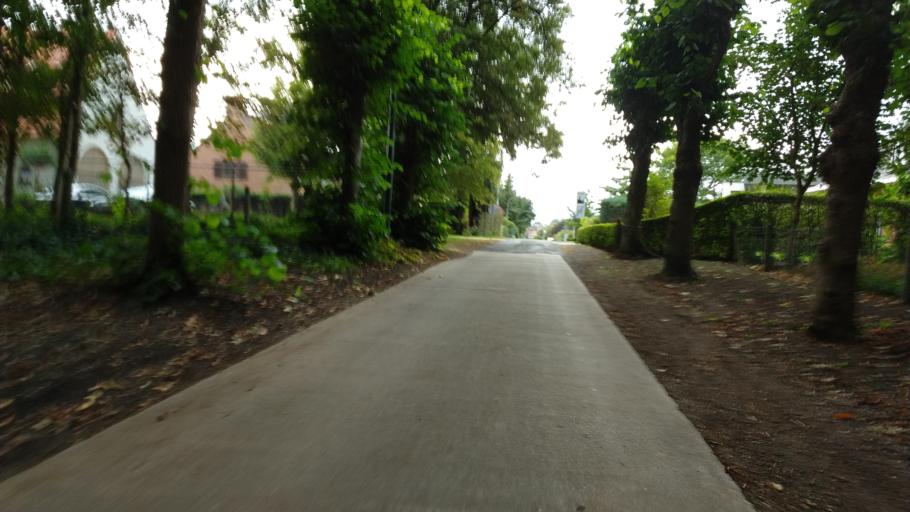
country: BE
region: Flanders
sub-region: Provincie Oost-Vlaanderen
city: Aalter
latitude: 51.0800
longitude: 3.4582
